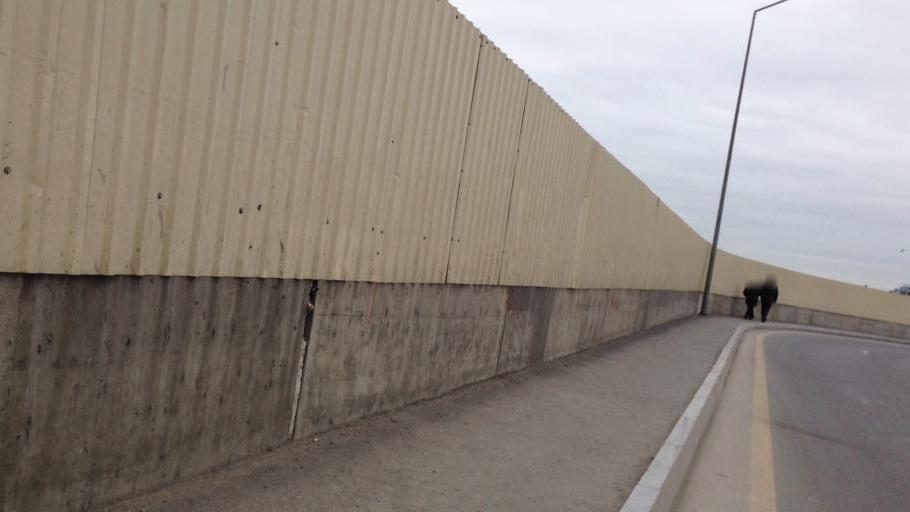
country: AZ
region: Baki
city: Baku
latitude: 40.3982
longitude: 49.8498
